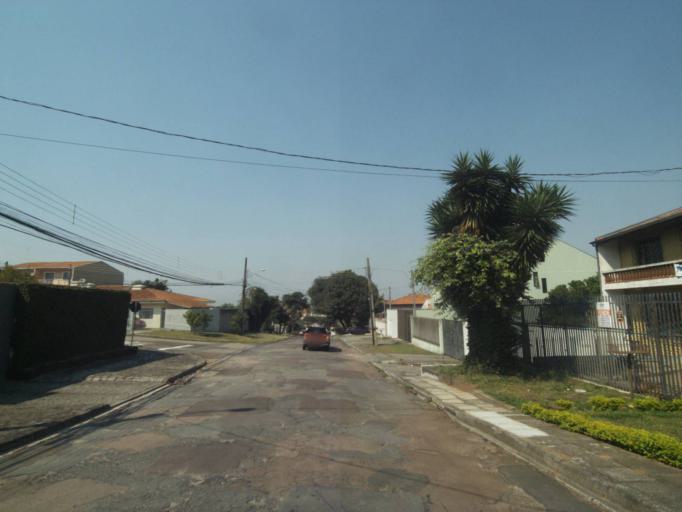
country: BR
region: Parana
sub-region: Sao Jose Dos Pinhais
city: Sao Jose dos Pinhais
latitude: -25.5080
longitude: -49.2749
